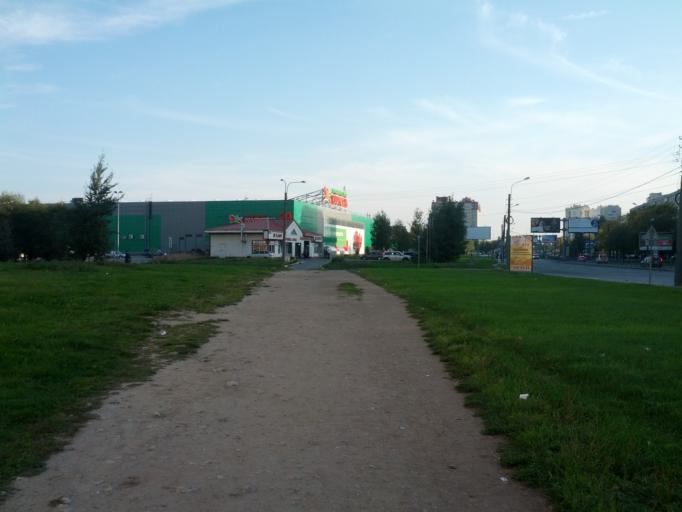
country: RU
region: Leningrad
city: Rybatskoye
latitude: 59.8970
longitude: 30.4923
